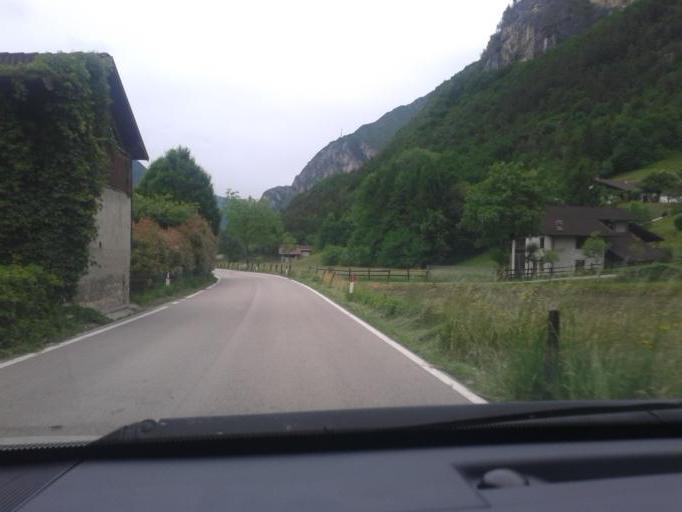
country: IT
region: Trentino-Alto Adige
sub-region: Provincia di Trento
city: Storo
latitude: 45.8353
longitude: 10.5650
